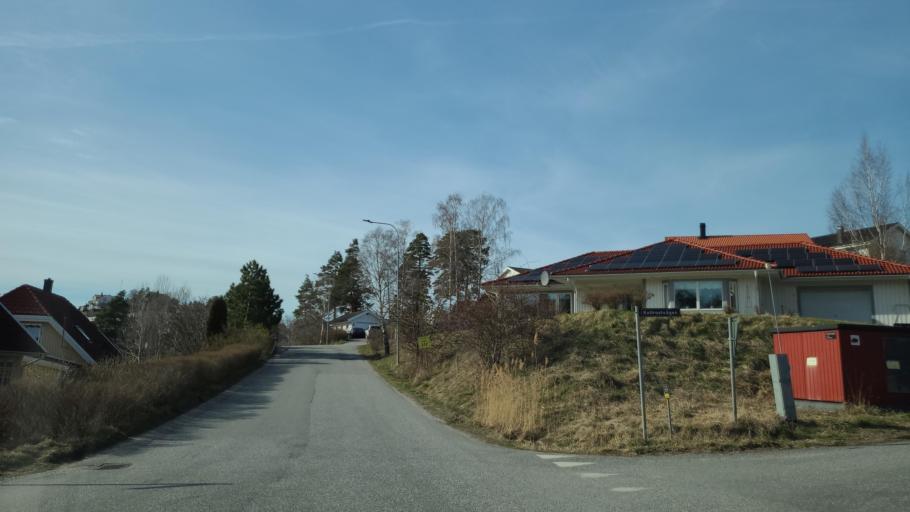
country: SE
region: Stockholm
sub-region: Ekero Kommun
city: Ekeroe
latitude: 59.2876
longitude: 17.7671
